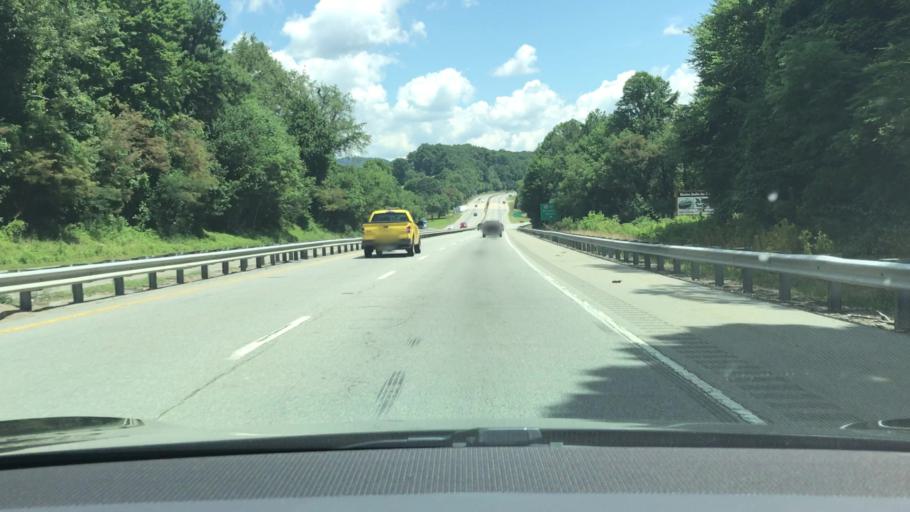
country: US
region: North Carolina
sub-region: Haywood County
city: Waynesville
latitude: 35.5028
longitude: -82.9968
